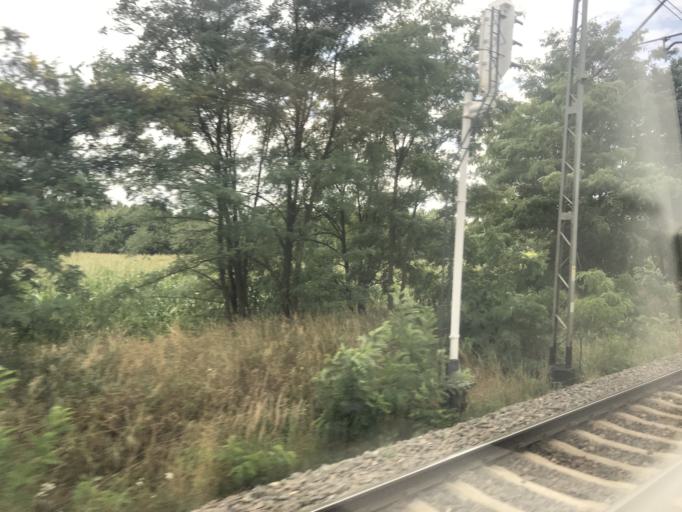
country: PL
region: Greater Poland Voivodeship
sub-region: Powiat poznanski
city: Dopiewo
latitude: 52.3466
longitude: 16.6107
